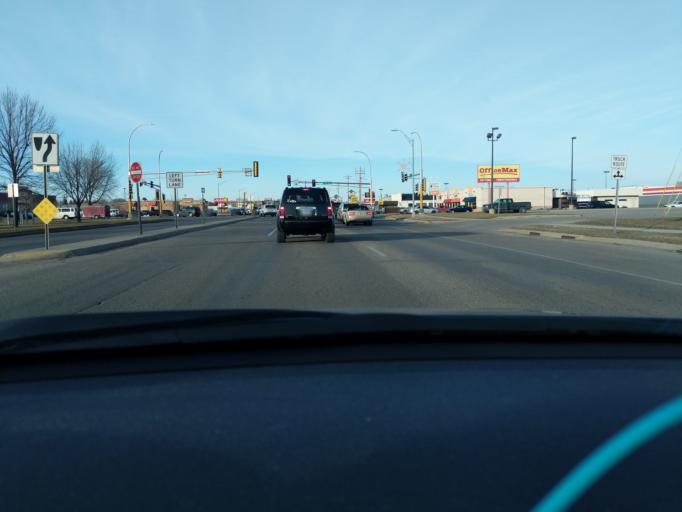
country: US
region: Minnesota
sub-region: Kandiyohi County
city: Willmar
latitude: 45.1026
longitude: -95.0426
